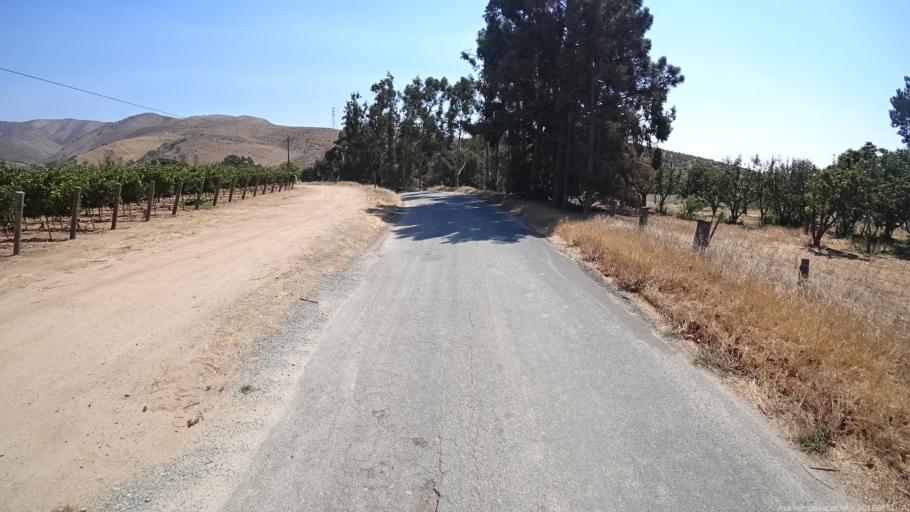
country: US
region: California
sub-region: Monterey County
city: Soledad
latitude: 36.4471
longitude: -121.3002
